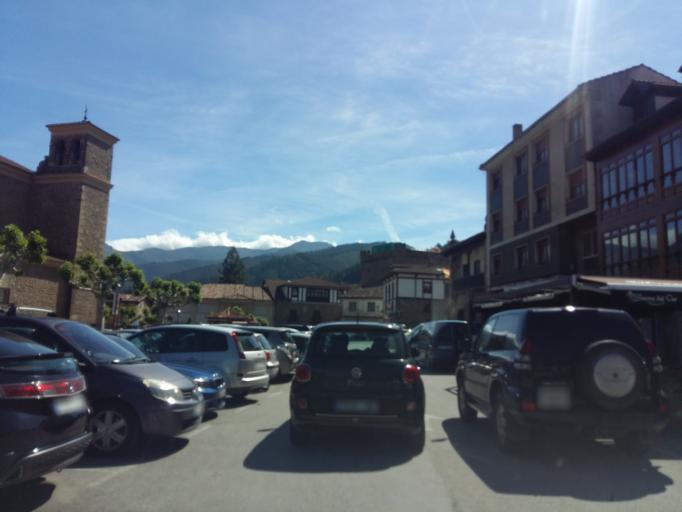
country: ES
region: Cantabria
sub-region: Provincia de Cantabria
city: Potes
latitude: 43.1541
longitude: -4.6251
